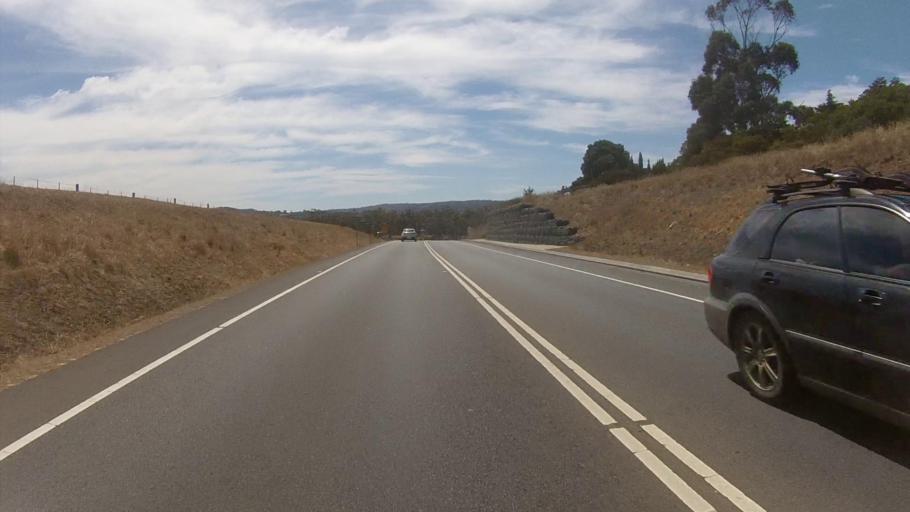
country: AU
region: Tasmania
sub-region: Kingborough
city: Kingston
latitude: -42.9895
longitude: 147.2860
